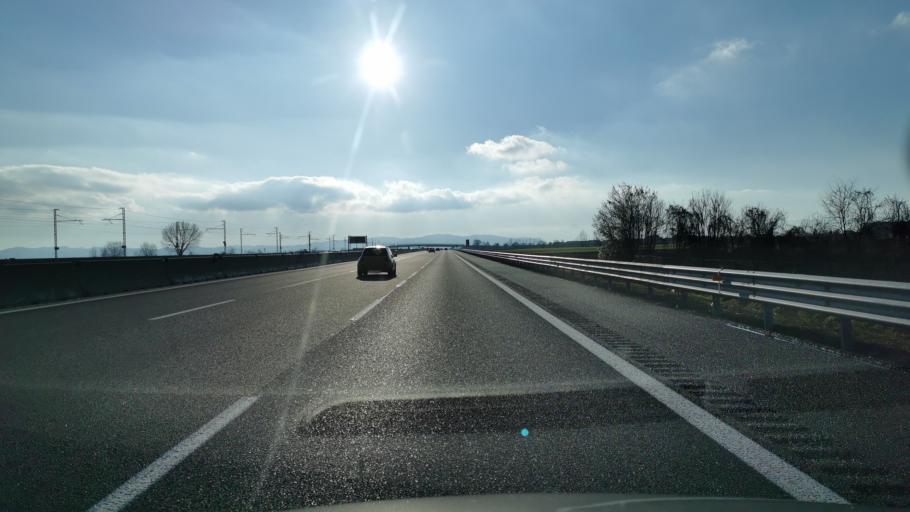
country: IT
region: Piedmont
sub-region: Provincia di Vercelli
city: Cigliano
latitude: 45.2742
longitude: 8.0215
